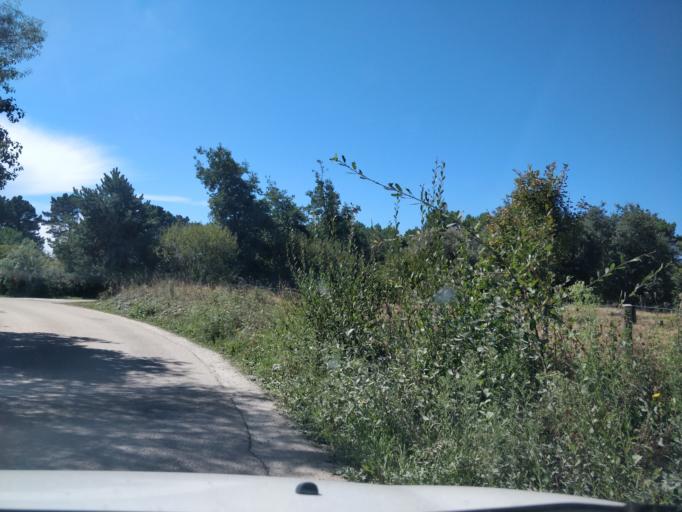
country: FR
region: Brittany
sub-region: Departement du Morbihan
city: Saint-Philibert
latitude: 47.5698
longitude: -3.0005
